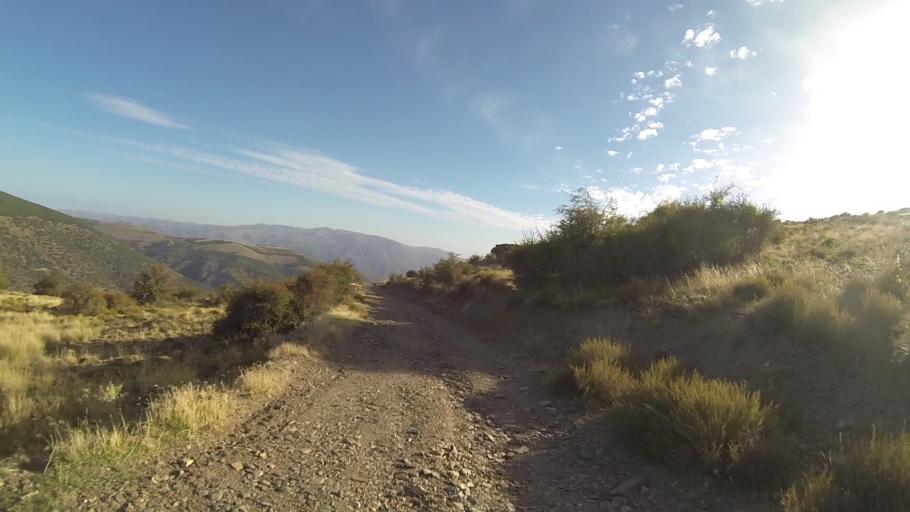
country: ES
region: Andalusia
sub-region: Provincia de Almeria
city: Laujar de Andarax
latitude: 37.0686
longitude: -2.8867
